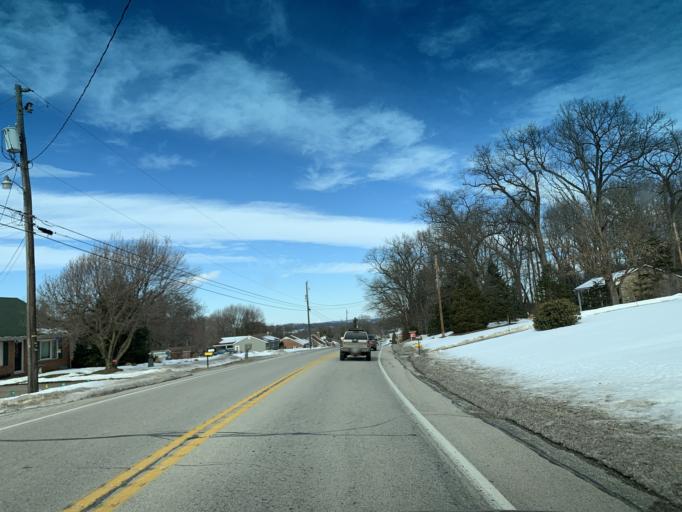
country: US
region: Pennsylvania
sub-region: York County
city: Jacobus
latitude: 39.8783
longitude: -76.7854
